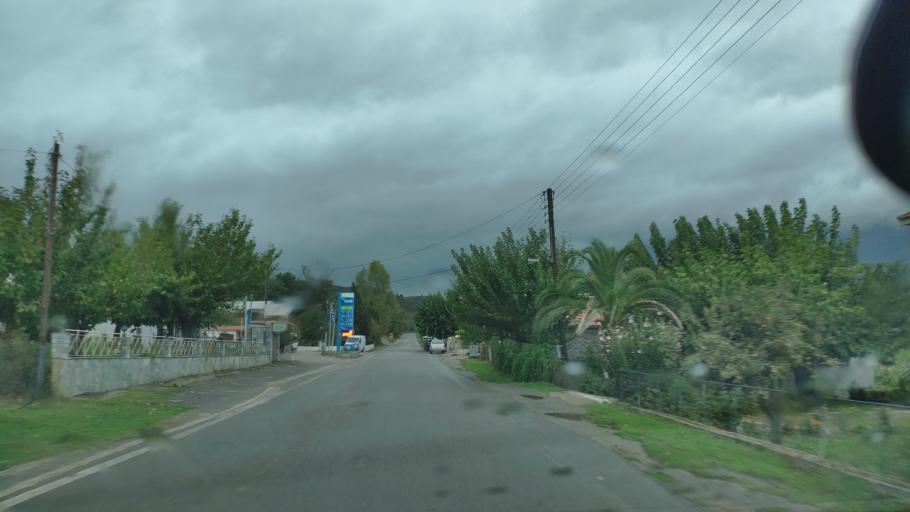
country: GR
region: West Greece
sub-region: Nomos Aitolias kai Akarnanias
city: Krikellos
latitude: 38.9986
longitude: 21.3114
